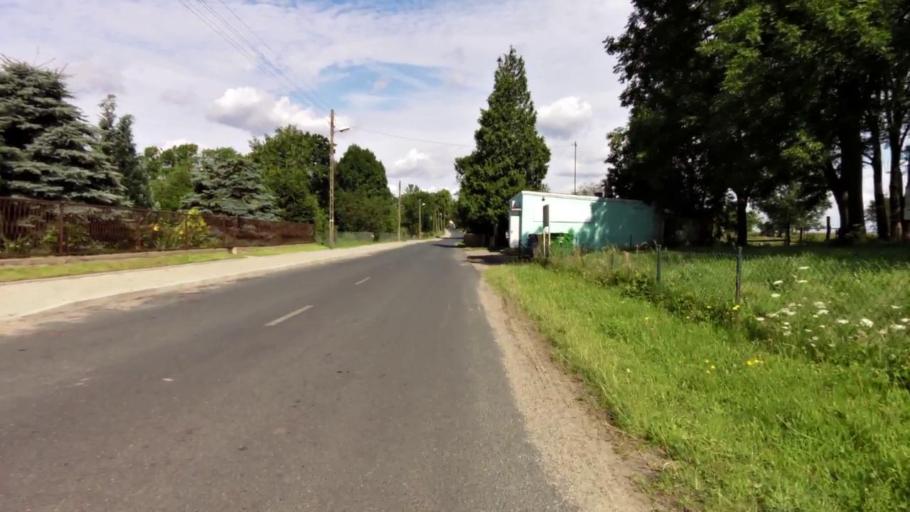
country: PL
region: West Pomeranian Voivodeship
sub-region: Powiat stargardzki
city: Dobrzany
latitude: 53.4076
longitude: 15.4292
